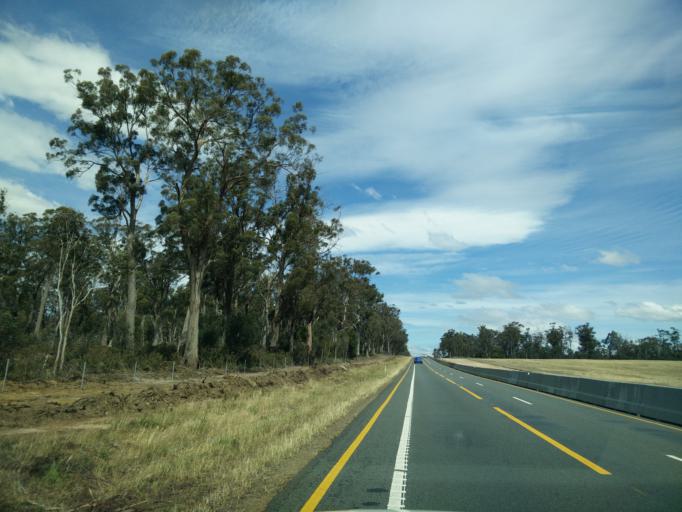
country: AU
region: Tasmania
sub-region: Northern Midlands
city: Evandale
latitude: -41.7476
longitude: 147.3389
